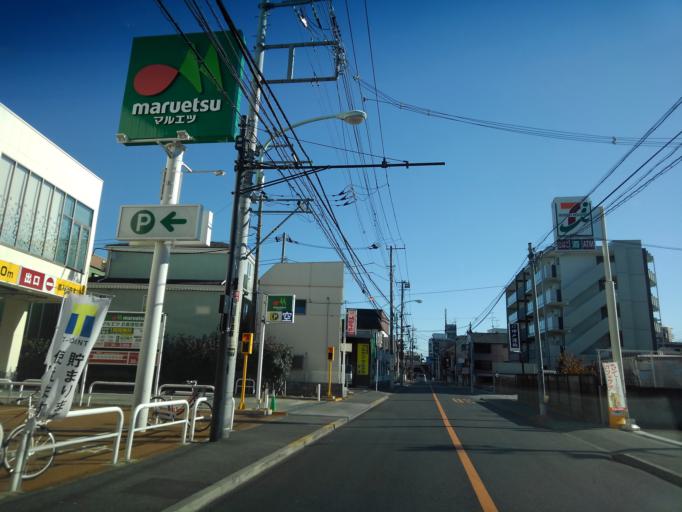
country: JP
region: Tokyo
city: Chofugaoka
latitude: 35.6626
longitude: 139.5218
